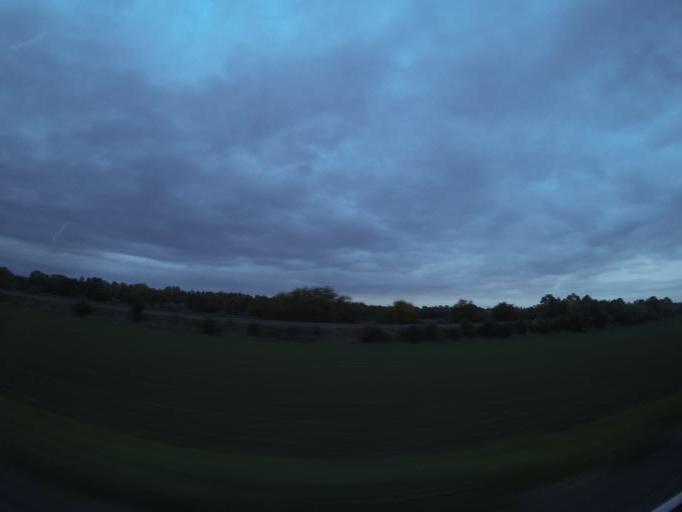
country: DE
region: Thuringia
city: Saara
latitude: 50.9248
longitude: 12.4297
